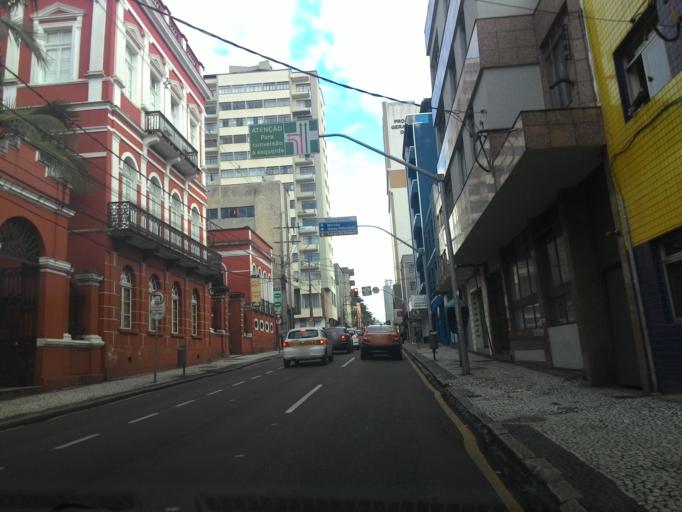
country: BR
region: Parana
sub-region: Curitiba
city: Curitiba
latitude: -25.4262
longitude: -49.2698
